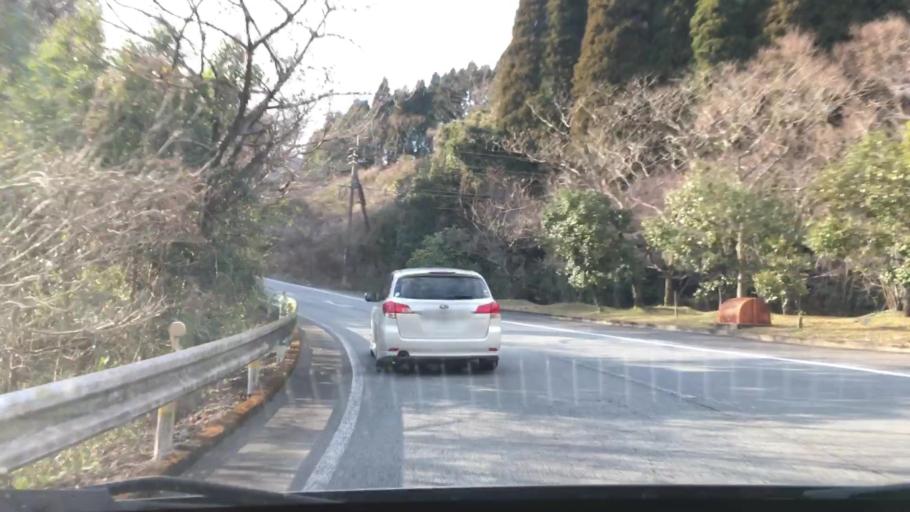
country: JP
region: Miyazaki
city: Miyazaki-shi
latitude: 31.7767
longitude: 131.3326
